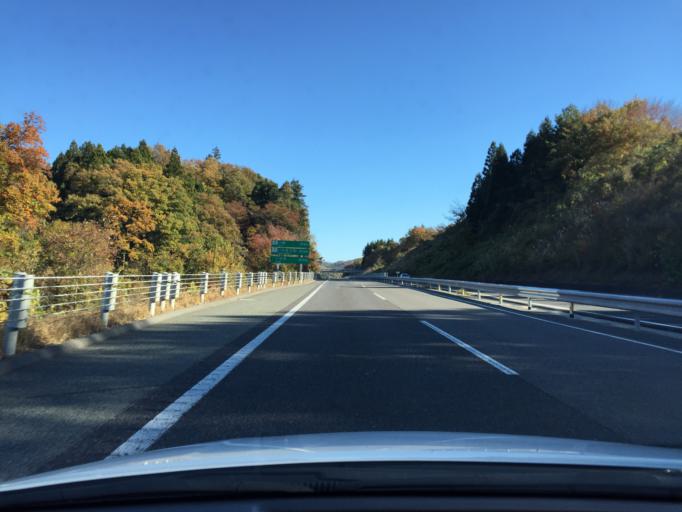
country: JP
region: Fukushima
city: Funehikimachi-funehiki
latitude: 37.4327
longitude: 140.5398
